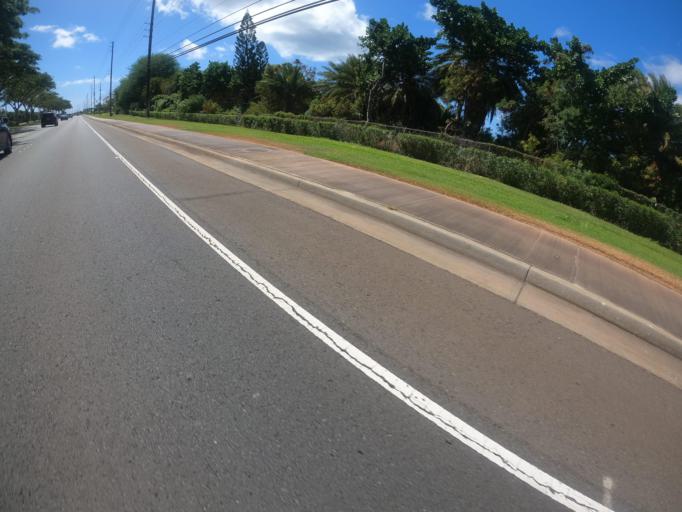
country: US
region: Hawaii
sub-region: Honolulu County
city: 'Ewa Gentry
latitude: 21.3391
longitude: -158.0246
